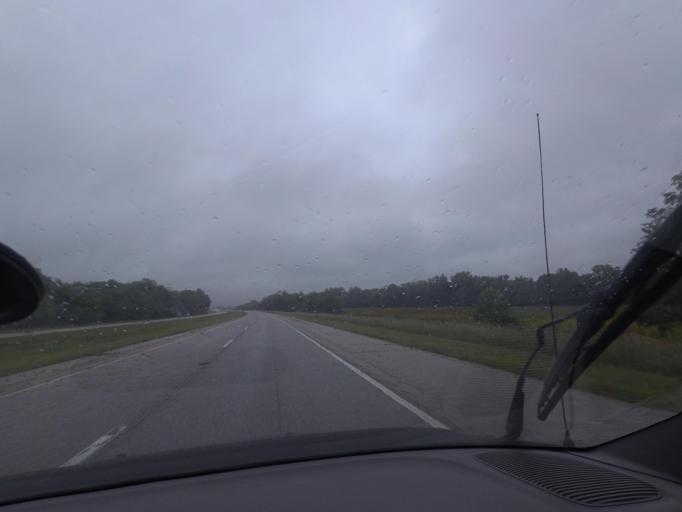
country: US
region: Illinois
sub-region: Pike County
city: Pittsfield
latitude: 39.6739
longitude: -90.8571
